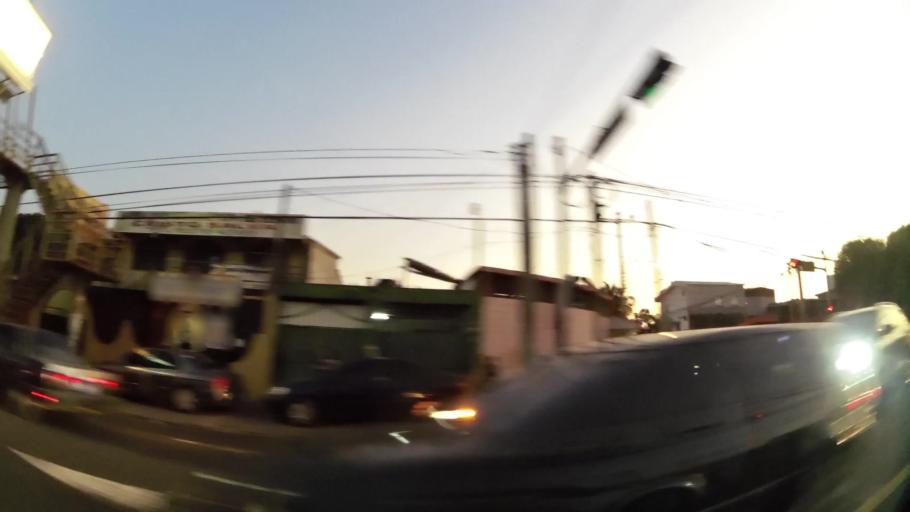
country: SV
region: La Libertad
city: Antiguo Cuscatlan
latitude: 13.6783
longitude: -89.2597
